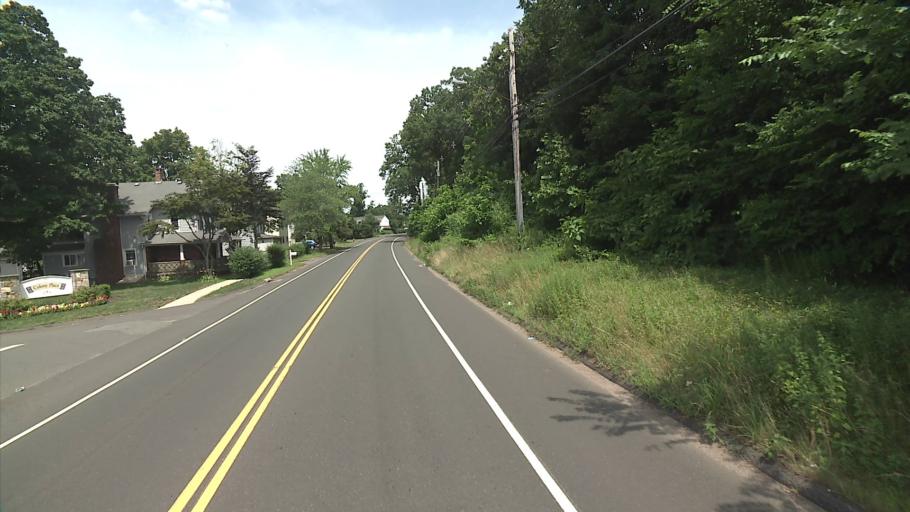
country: US
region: Connecticut
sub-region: New Haven County
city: Meriden
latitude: 41.5008
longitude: -72.8163
